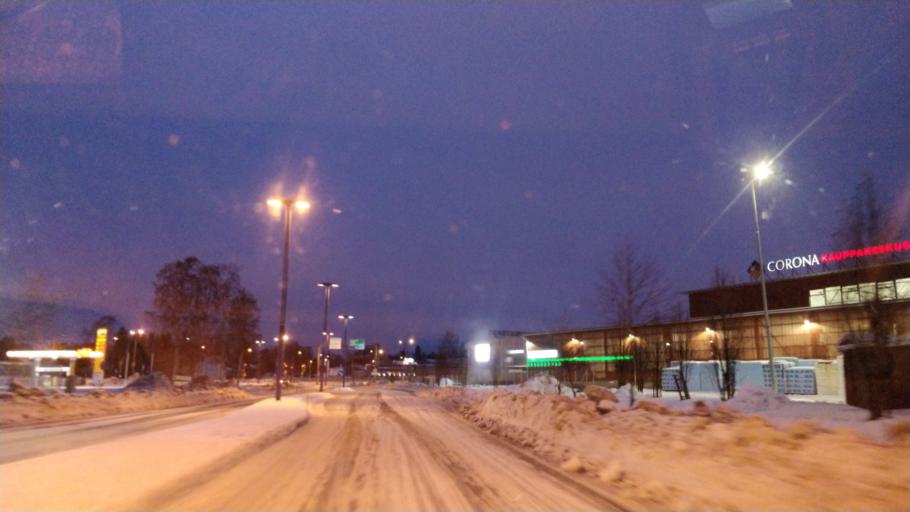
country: FI
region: Lapland
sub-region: Kemi-Tornio
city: Kemi
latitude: 65.7414
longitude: 24.5770
